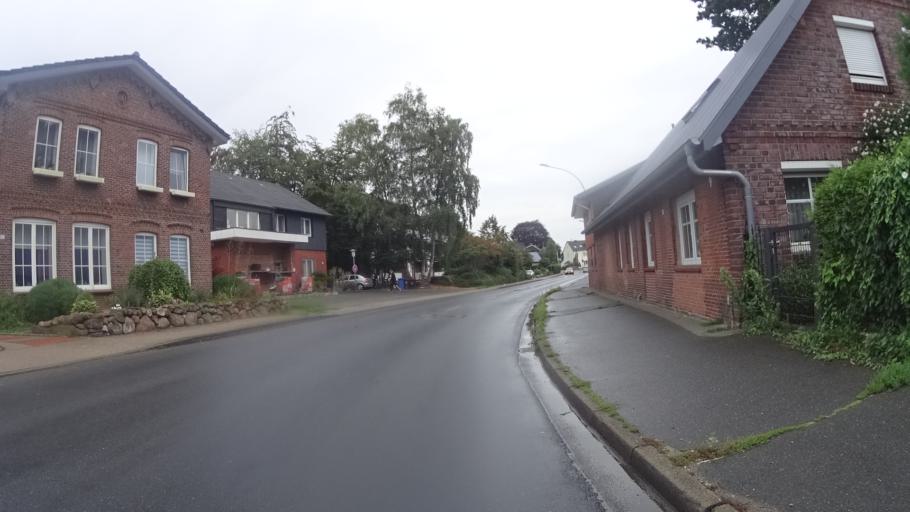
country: DE
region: Schleswig-Holstein
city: Alveslohe
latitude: 53.7867
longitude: 9.9122
